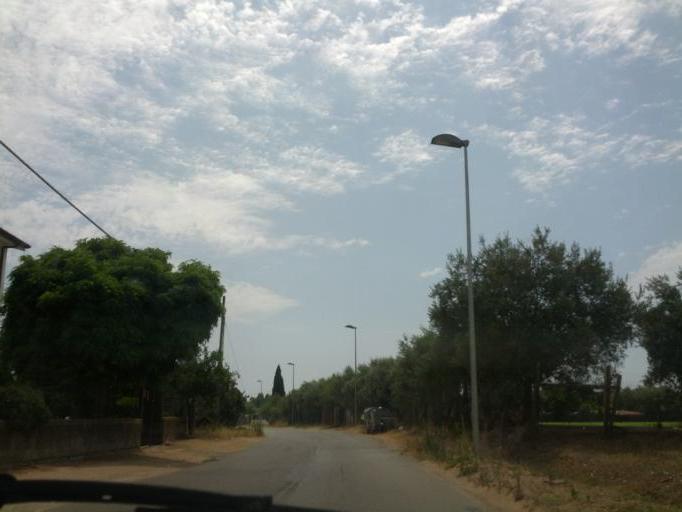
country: IT
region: Latium
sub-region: Provincia di Latina
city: Sperlonga
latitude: 41.2880
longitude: 13.3899
